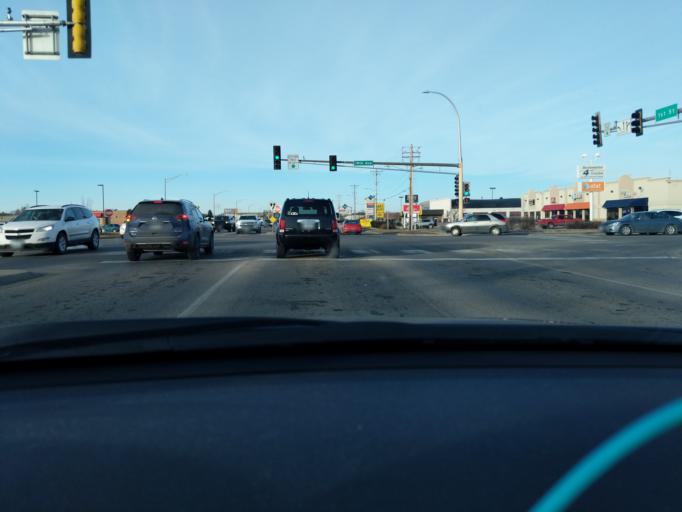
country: US
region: Minnesota
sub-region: Kandiyohi County
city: Willmar
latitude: 45.1031
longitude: -95.0426
